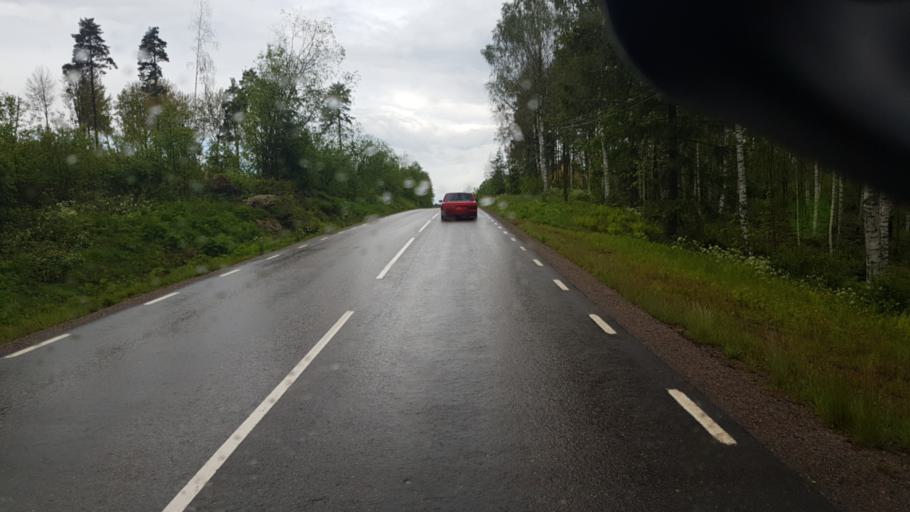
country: SE
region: Vaermland
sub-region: Eda Kommun
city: Amotfors
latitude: 59.7498
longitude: 12.3697
